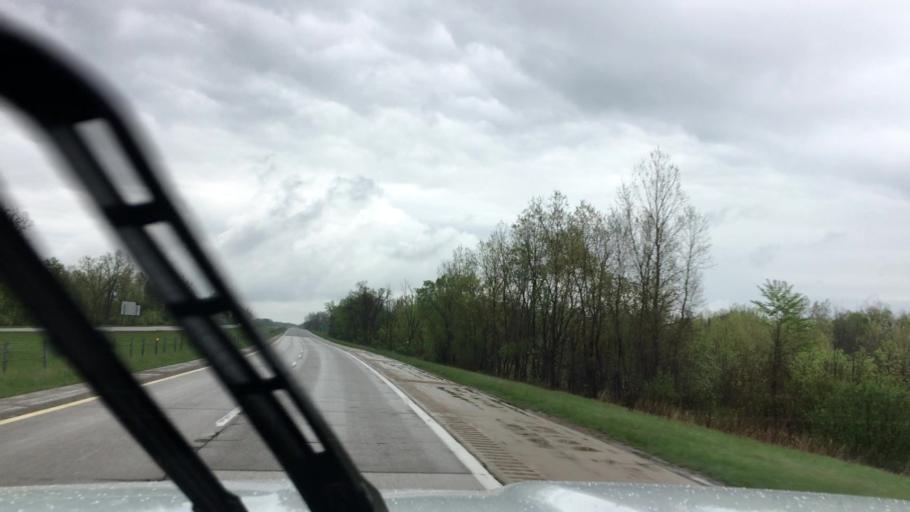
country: US
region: Michigan
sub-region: Shiawassee County
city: Perry
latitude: 42.8436
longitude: -84.1956
